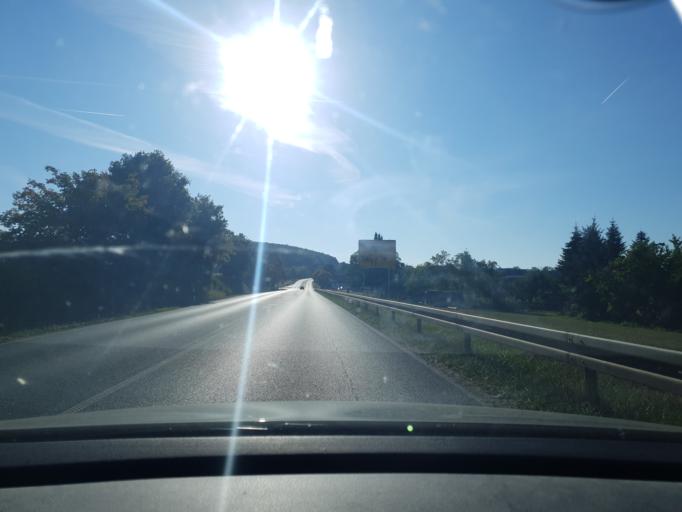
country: DE
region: Hesse
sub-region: Regierungsbezirk Giessen
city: Hoernsheim
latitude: 50.4794
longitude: 8.6151
